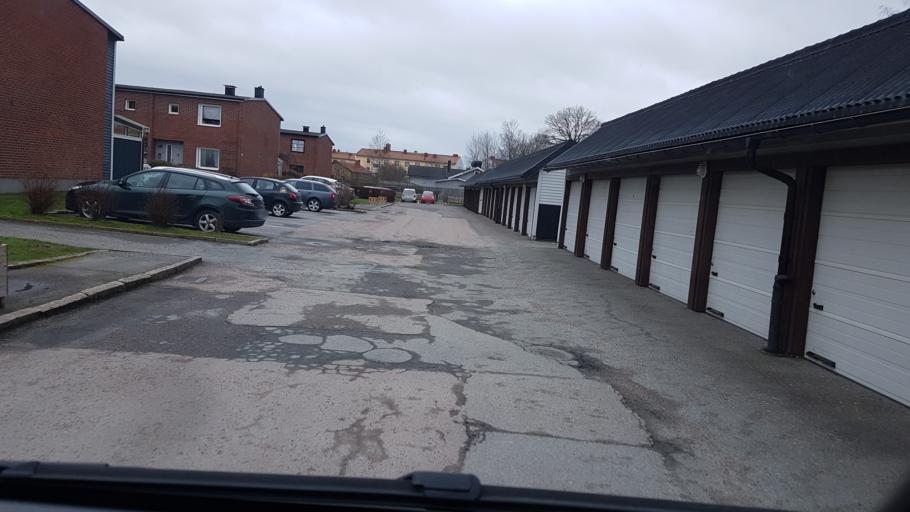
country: SE
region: Vaestra Goetaland
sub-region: Lerums Kommun
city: Stenkullen
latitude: 57.7902
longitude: 12.3074
